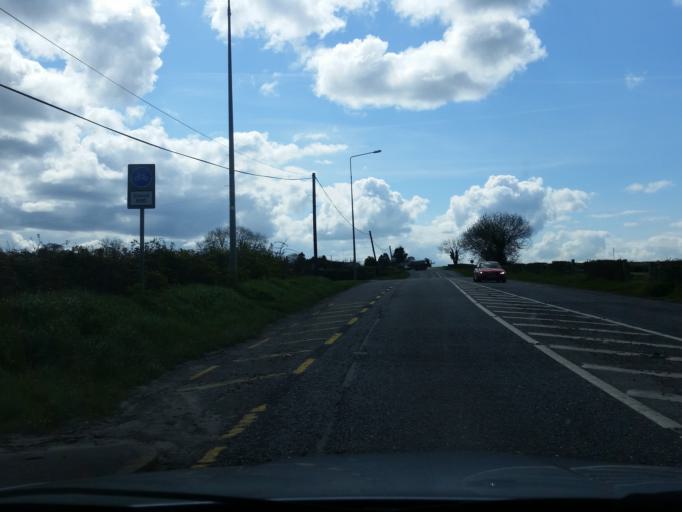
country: IE
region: Leinster
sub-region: An Mhi
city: Slane
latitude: 53.6984
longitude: -6.5380
